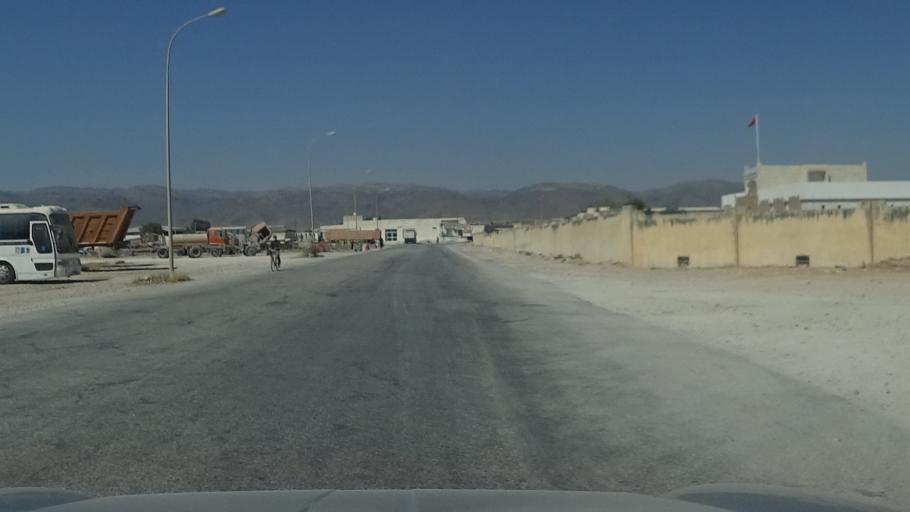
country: OM
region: Zufar
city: Salalah
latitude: 17.0266
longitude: 54.0441
